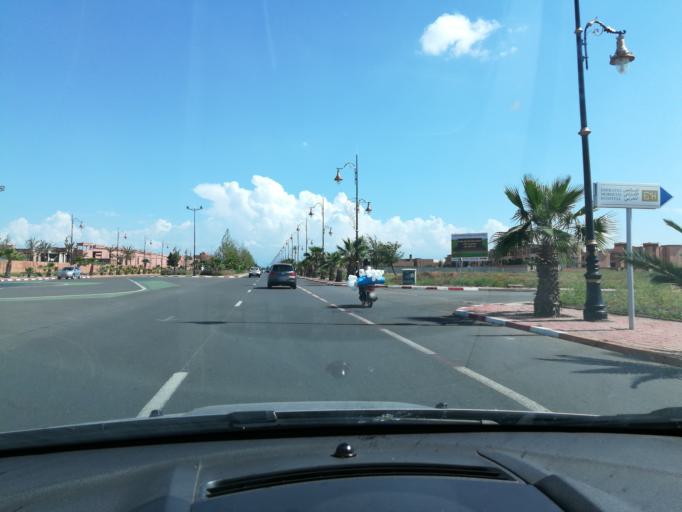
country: MA
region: Marrakech-Tensift-Al Haouz
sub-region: Marrakech
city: Marrakesh
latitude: 31.5829
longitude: -7.9854
